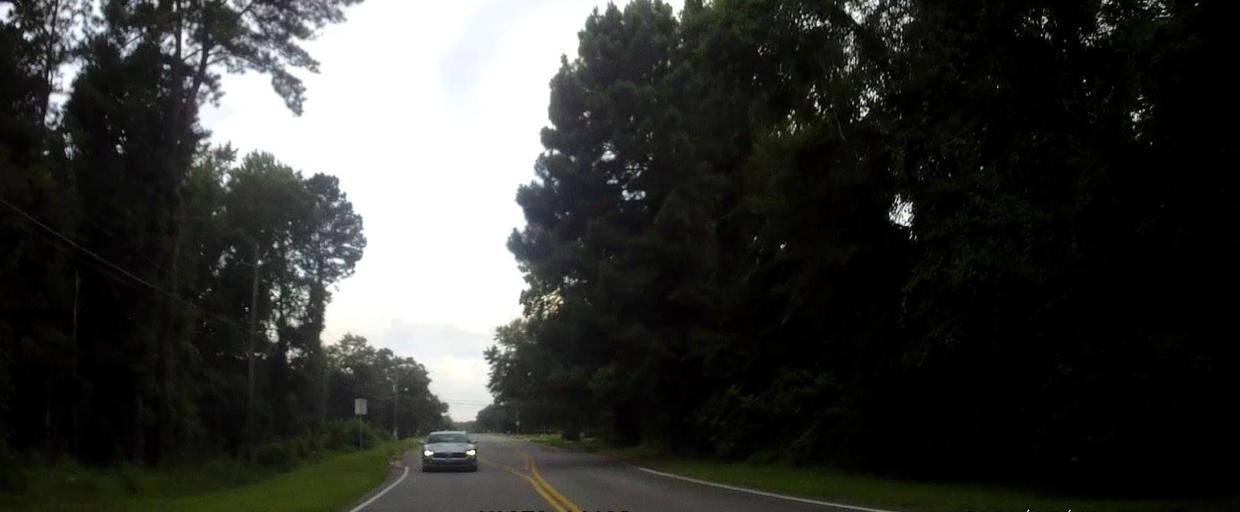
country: US
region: Georgia
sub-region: Laurens County
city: Dublin
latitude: 32.5672
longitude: -82.9110
